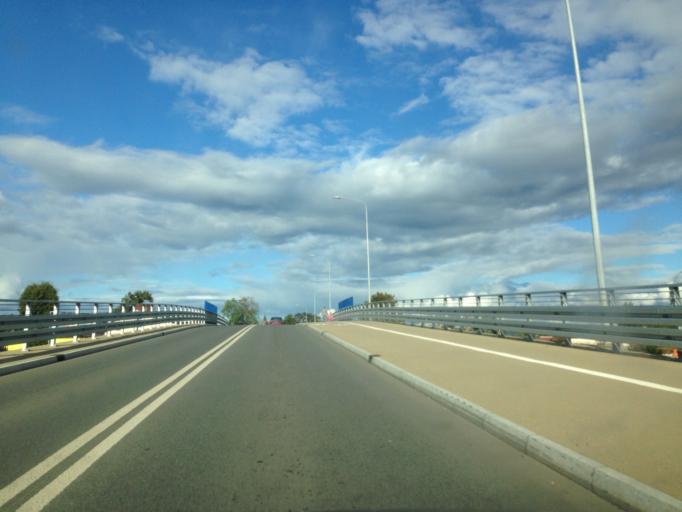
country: PL
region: Warmian-Masurian Voivodeship
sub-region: Powiat ilawski
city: Susz
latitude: 53.7091
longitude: 19.3310
